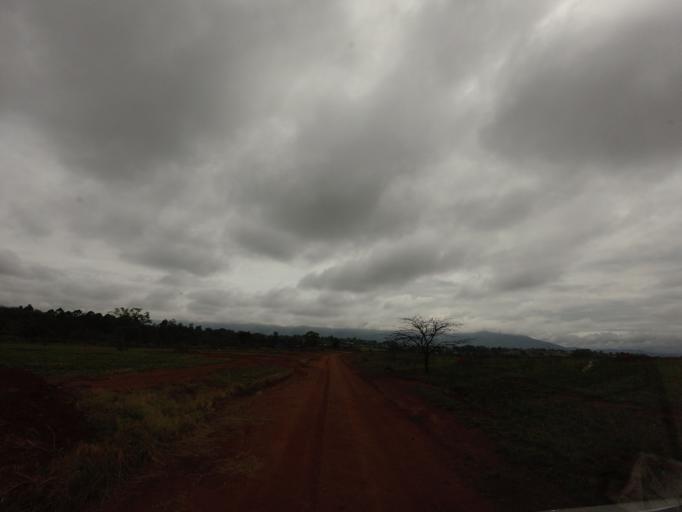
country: SZ
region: Hhohho
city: Lobamba
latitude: -26.4620
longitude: 31.1863
